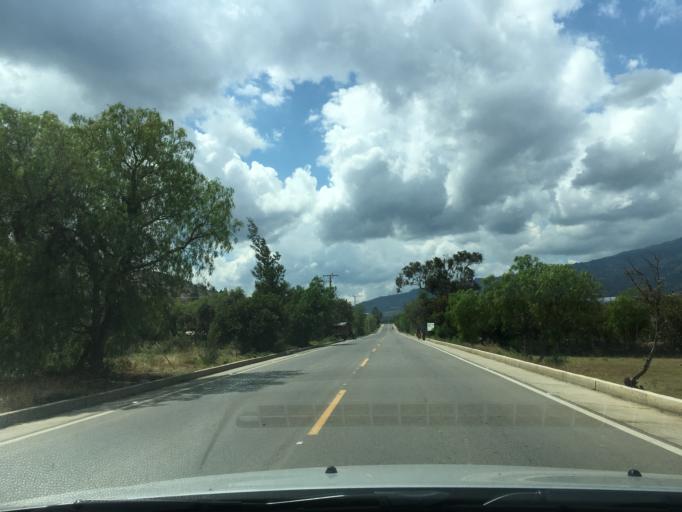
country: CO
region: Boyaca
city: Sutamarchan
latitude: 5.6230
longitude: -73.5973
